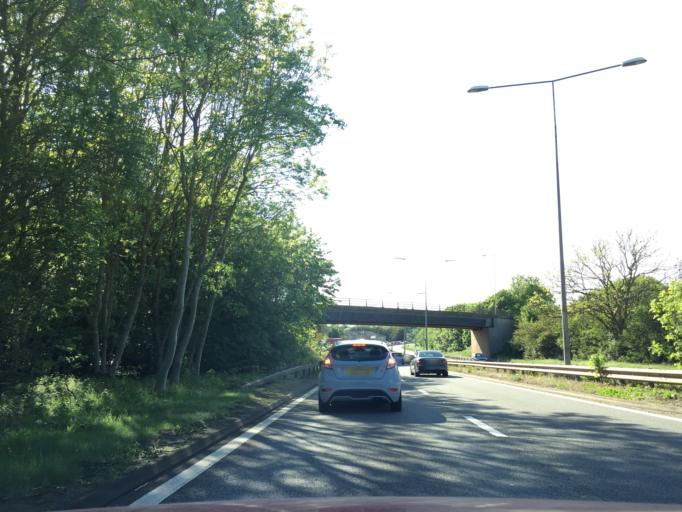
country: GB
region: England
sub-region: Warwickshire
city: Ryton on Dunsmore
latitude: 52.3730
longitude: -1.4542
